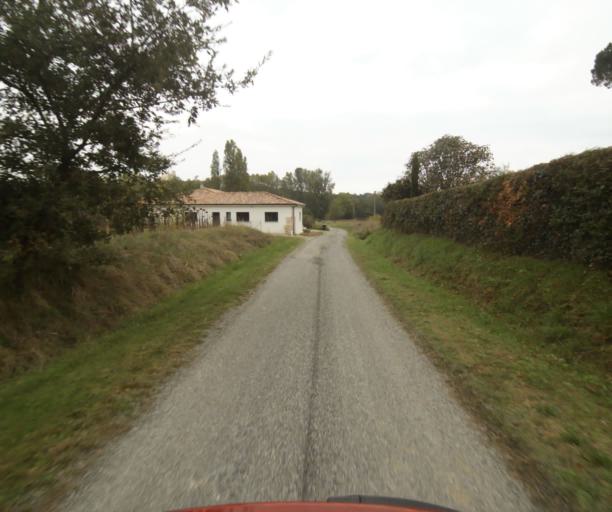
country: FR
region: Midi-Pyrenees
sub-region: Departement de la Haute-Garonne
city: Grenade
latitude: 43.7792
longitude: 1.2307
